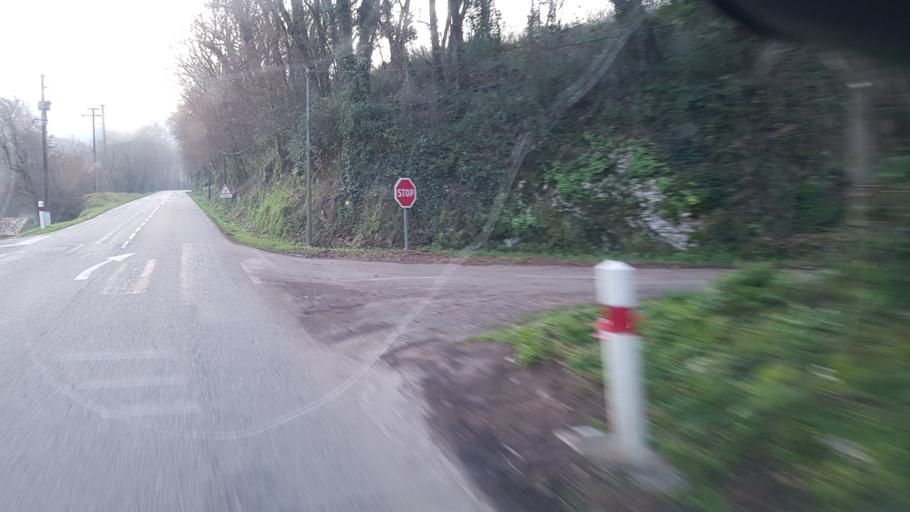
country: FR
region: Midi-Pyrenees
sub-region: Departement du Tarn-et-Garonne
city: Montricoux
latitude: 44.0648
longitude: 1.6605
